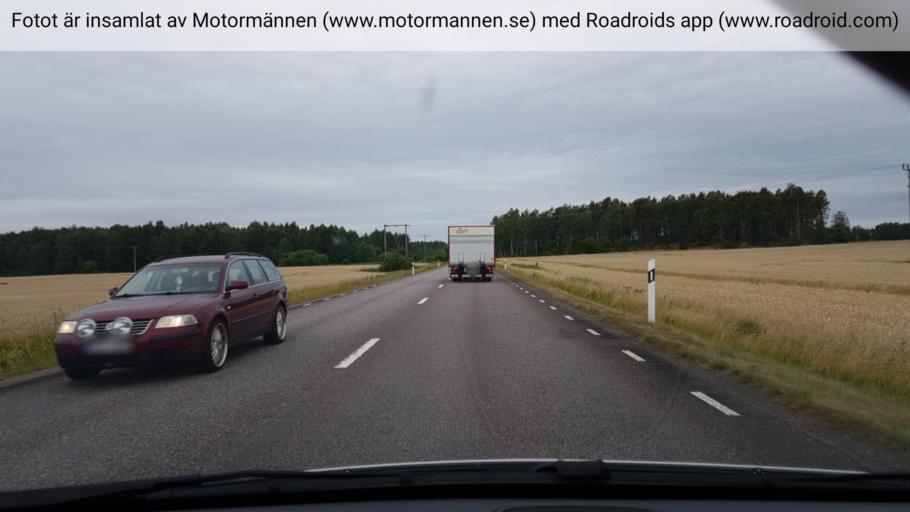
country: SE
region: Vaestra Goetaland
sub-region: Karlsborgs Kommun
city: Molltorp
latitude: 58.4915
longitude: 14.4370
